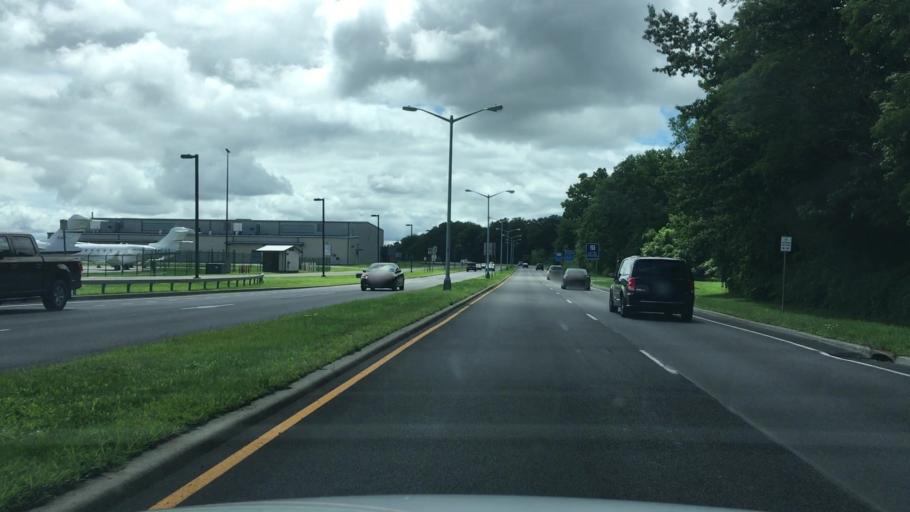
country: US
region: New York
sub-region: Albany County
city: Colonie
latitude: 42.7401
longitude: -73.8084
